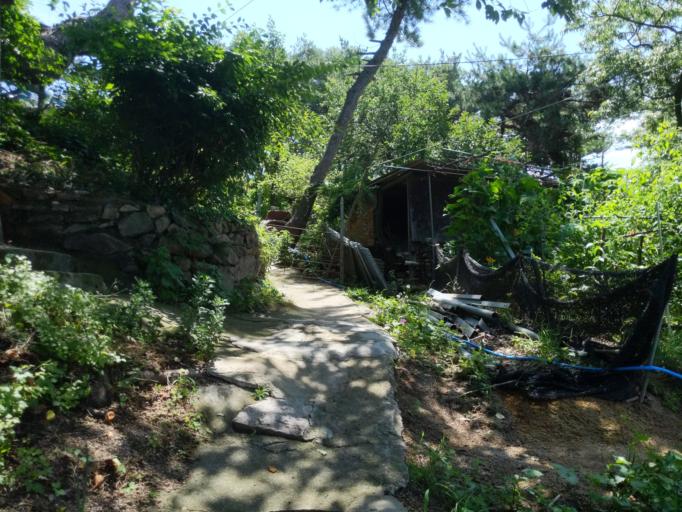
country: KR
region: Seoul
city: Seoul
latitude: 37.6024
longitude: 126.9648
